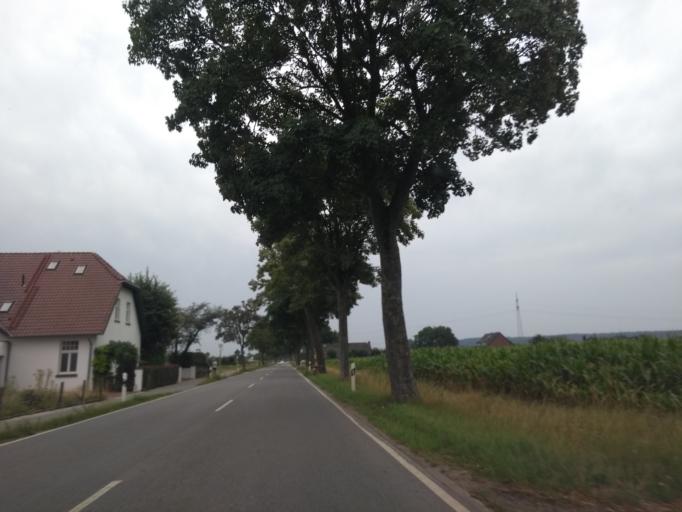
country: DE
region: North Rhine-Westphalia
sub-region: Regierungsbezirk Dusseldorf
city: Kleve
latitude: 51.8220
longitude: 6.1131
